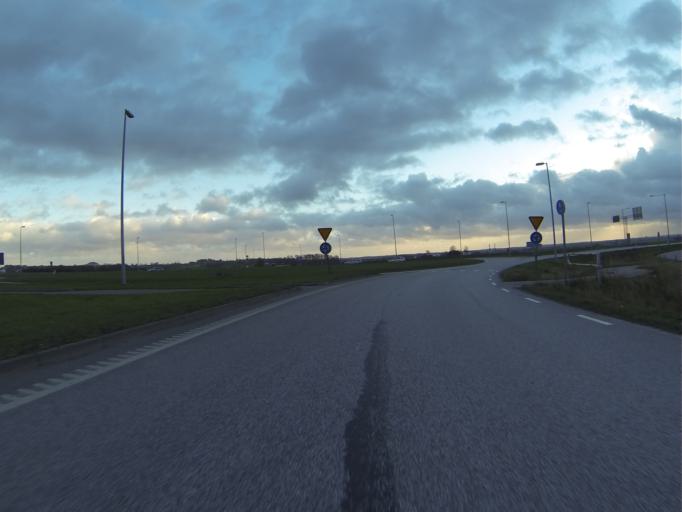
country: SE
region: Skane
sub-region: Lunds Kommun
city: Genarp
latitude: 55.6619
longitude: 13.3333
